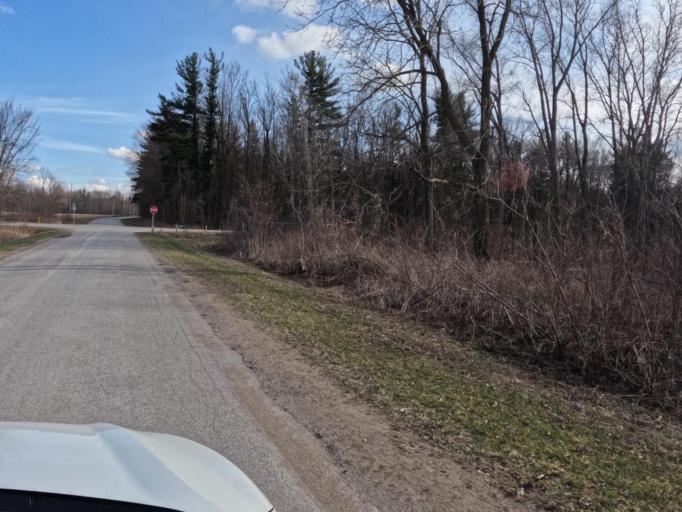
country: CA
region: Ontario
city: Brant
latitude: 42.9933
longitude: -80.4093
